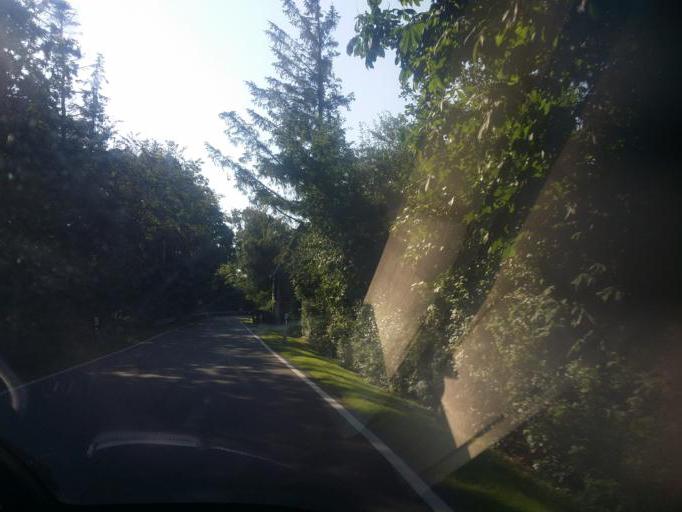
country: DE
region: Schleswig-Holstein
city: Galmsbull
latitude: 54.7862
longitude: 8.7321
